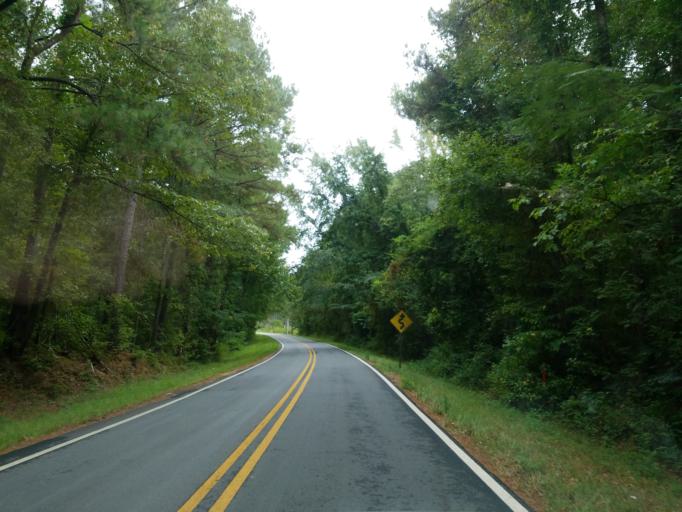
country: US
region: Georgia
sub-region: Monroe County
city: Forsyth
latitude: 32.9100
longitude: -83.8950
